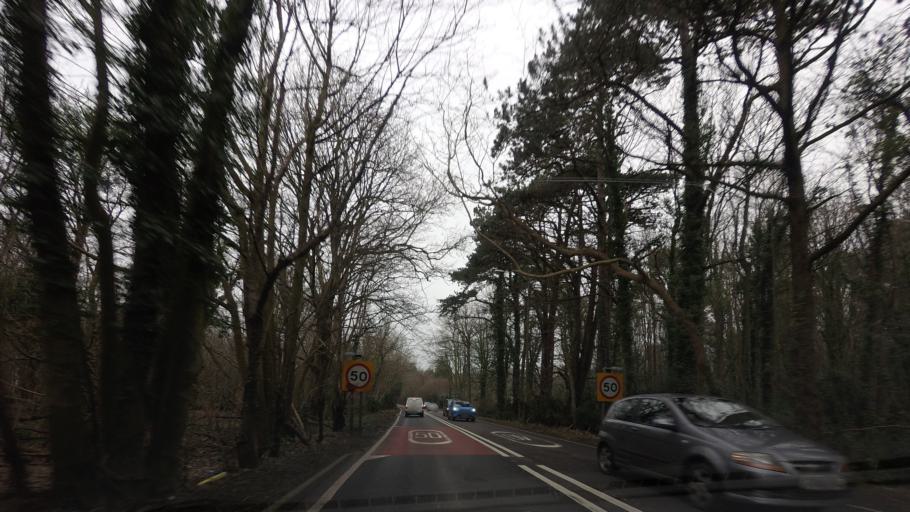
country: GB
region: England
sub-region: East Sussex
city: Saint Leonards-on-Sea
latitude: 50.8935
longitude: 0.5563
